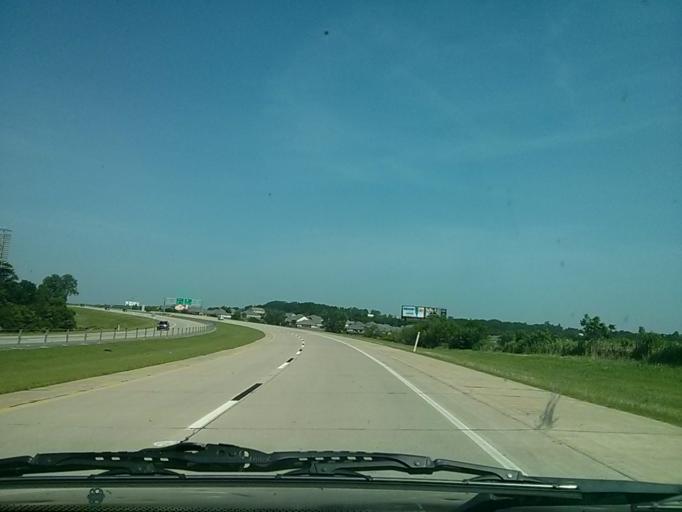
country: US
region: Oklahoma
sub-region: Creek County
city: Sapulpa
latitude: 36.0265
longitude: -96.0775
